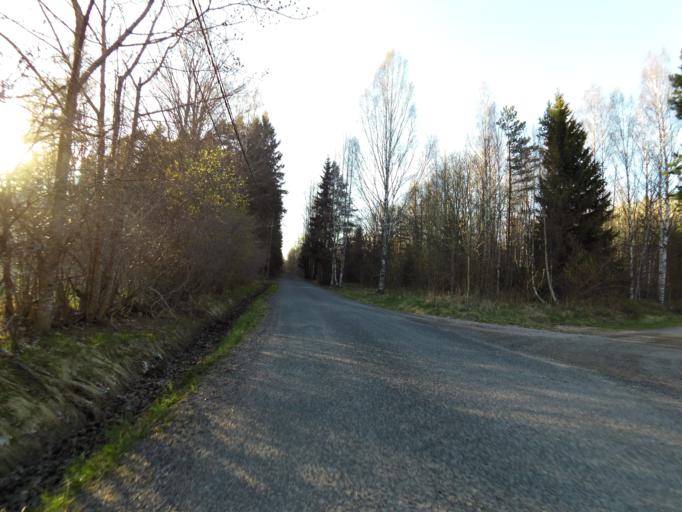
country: FI
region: Uusimaa
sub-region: Helsinki
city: Espoo
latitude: 60.1791
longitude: 24.6900
